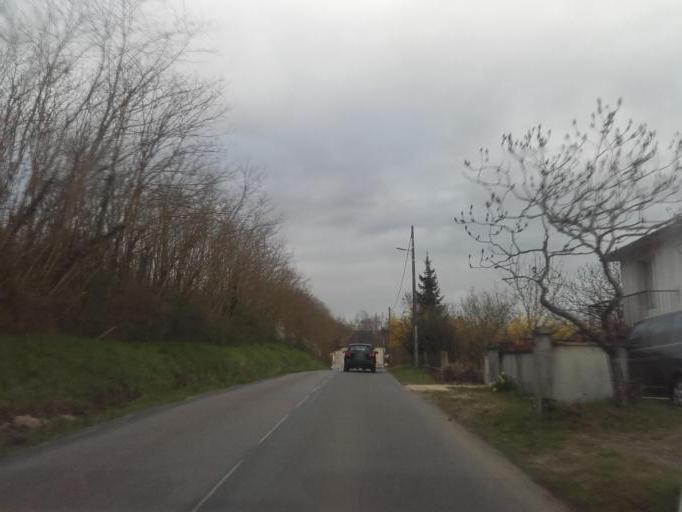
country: FR
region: Bourgogne
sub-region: Departement de la Cote-d'Or
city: Nolay
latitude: 46.9127
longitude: 4.6414
